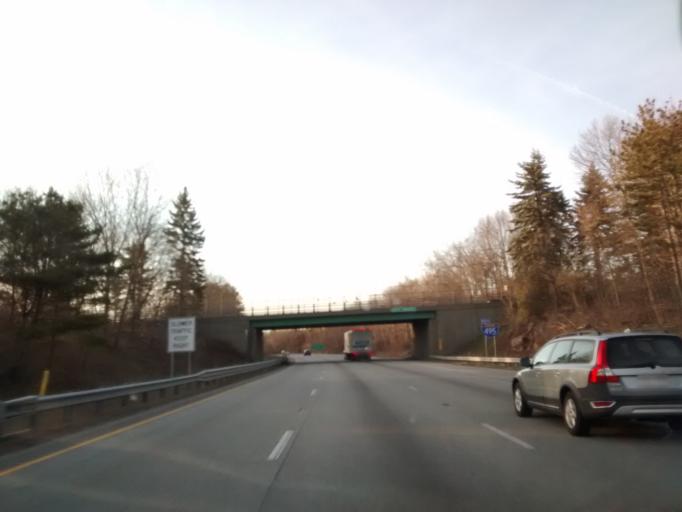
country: US
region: Massachusetts
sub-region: Middlesex County
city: Marlborough
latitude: 42.3467
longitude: -71.5751
